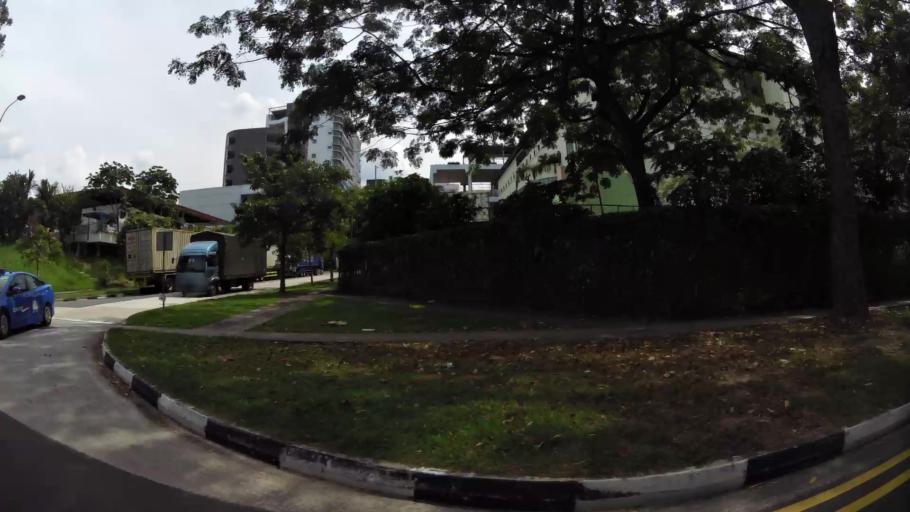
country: MY
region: Johor
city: Johor Bahru
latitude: 1.4115
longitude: 103.7571
